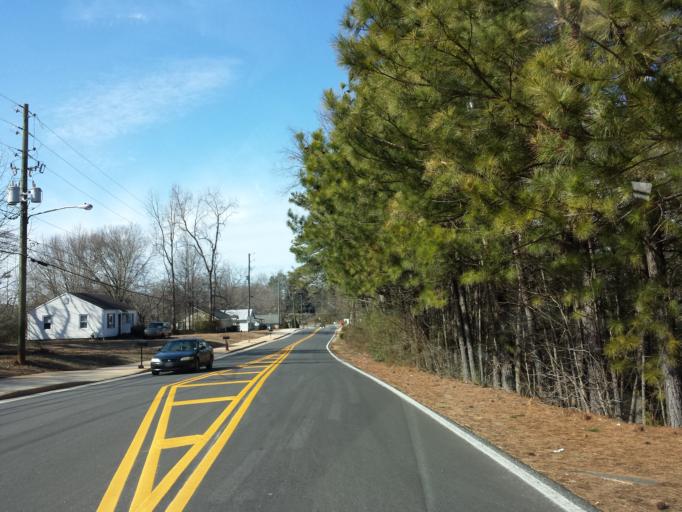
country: US
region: Georgia
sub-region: Cobb County
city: Kennesaw
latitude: 34.0210
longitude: -84.6116
